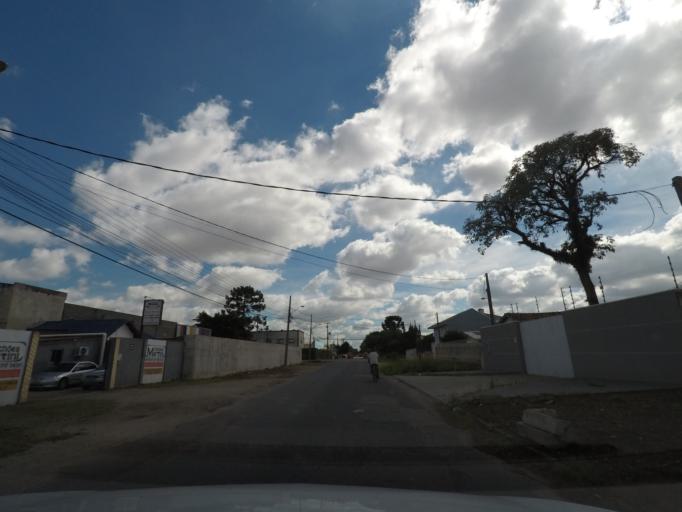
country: BR
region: Parana
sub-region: Sao Jose Dos Pinhais
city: Sao Jose dos Pinhais
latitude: -25.5078
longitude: -49.2248
